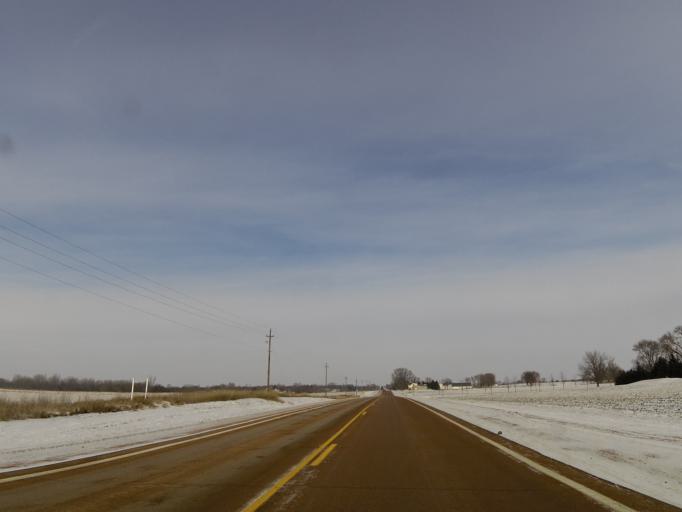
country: US
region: Minnesota
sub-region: McLeod County
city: Lester Prairie
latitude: 44.8955
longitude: -93.9713
